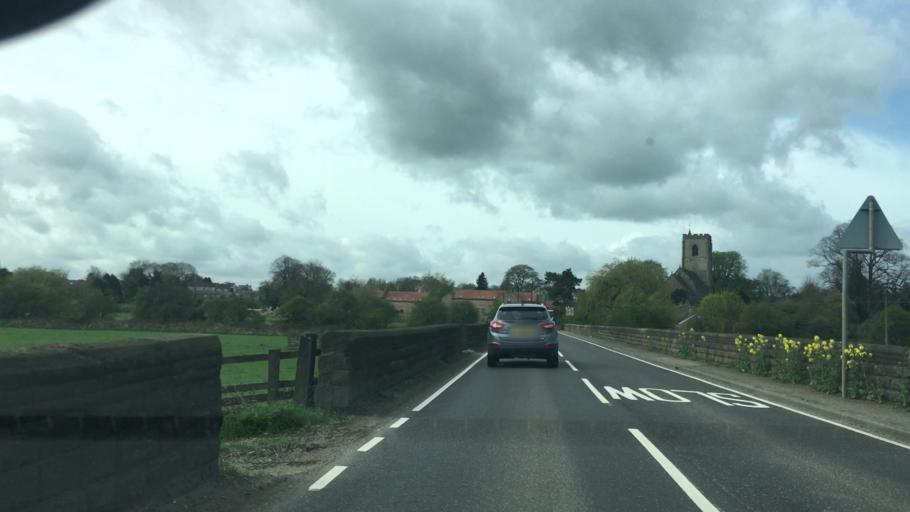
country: GB
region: England
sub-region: City and Borough of Leeds
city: Collingham
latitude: 53.9555
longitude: -1.4417
